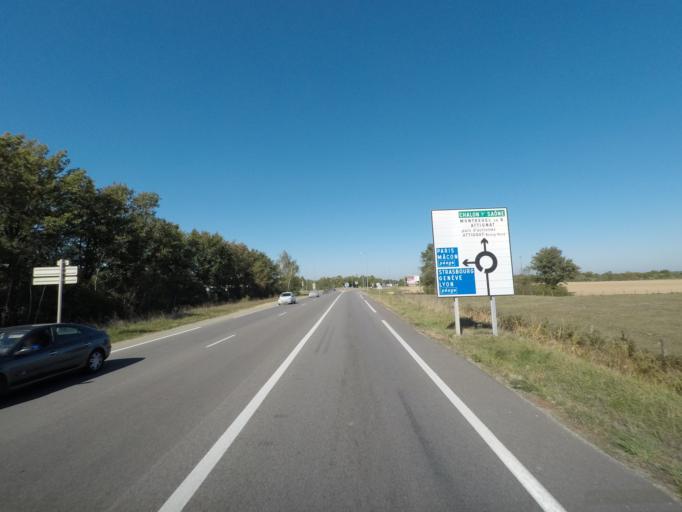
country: FR
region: Rhone-Alpes
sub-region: Departement de l'Ain
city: Attignat
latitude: 46.2582
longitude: 5.1779
